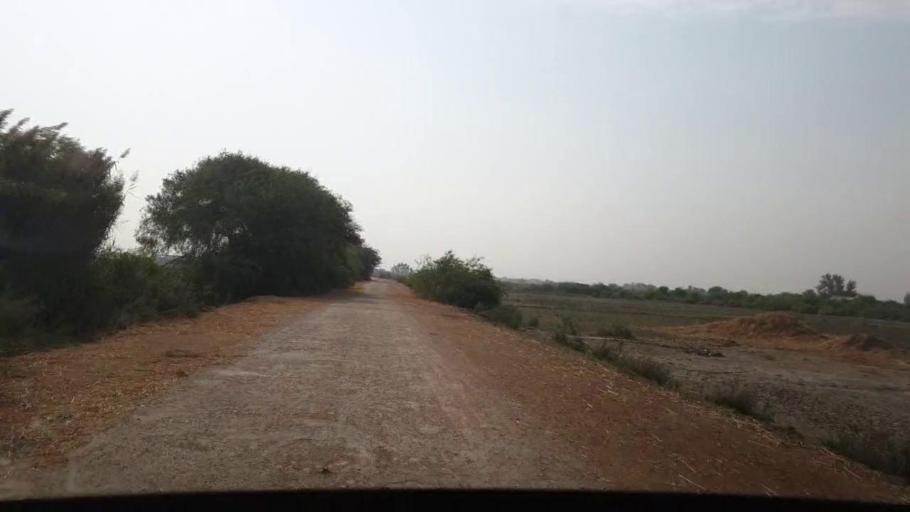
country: PK
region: Sindh
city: Chuhar Jamali
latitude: 24.3784
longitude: 67.9408
